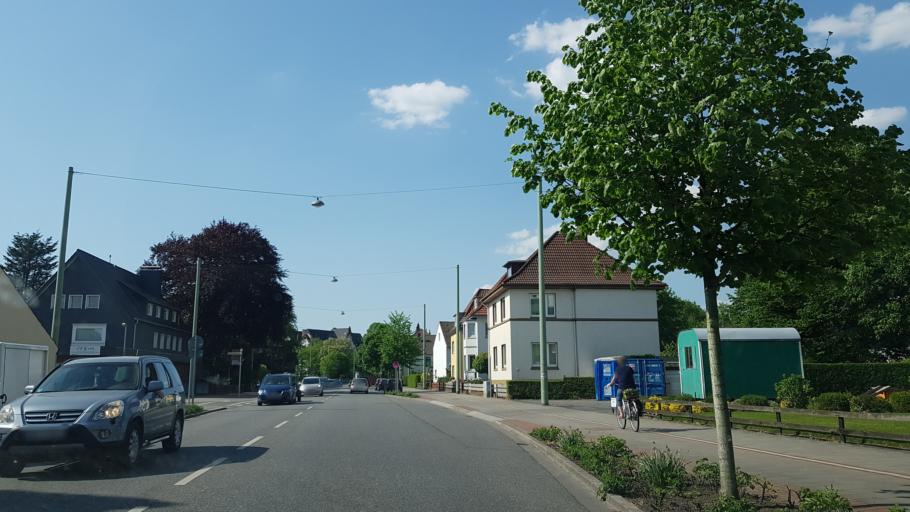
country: DE
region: Bremen
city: Bremerhaven
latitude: 53.5725
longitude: 8.5944
